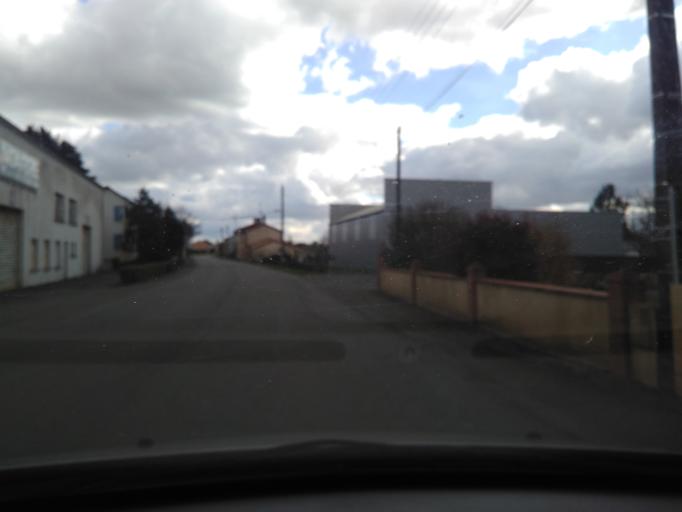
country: FR
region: Pays de la Loire
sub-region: Departement de la Vendee
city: Saint-Martin-des-Noyers
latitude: 46.7295
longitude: -1.1815
